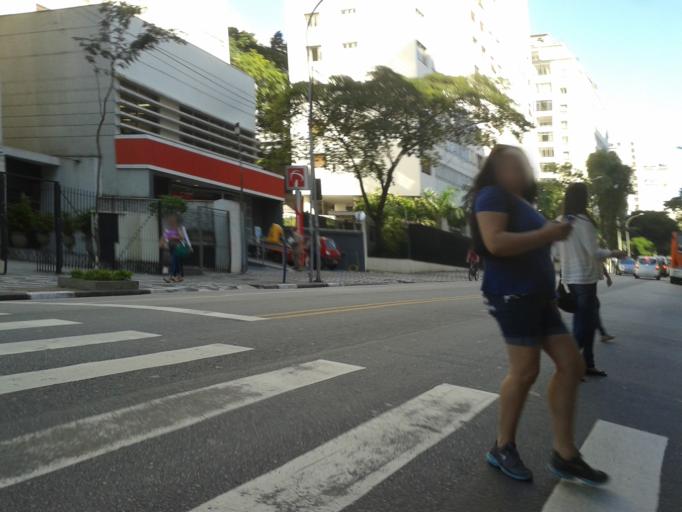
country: BR
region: Sao Paulo
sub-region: Sao Paulo
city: Sao Paulo
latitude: -23.5428
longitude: -46.6562
